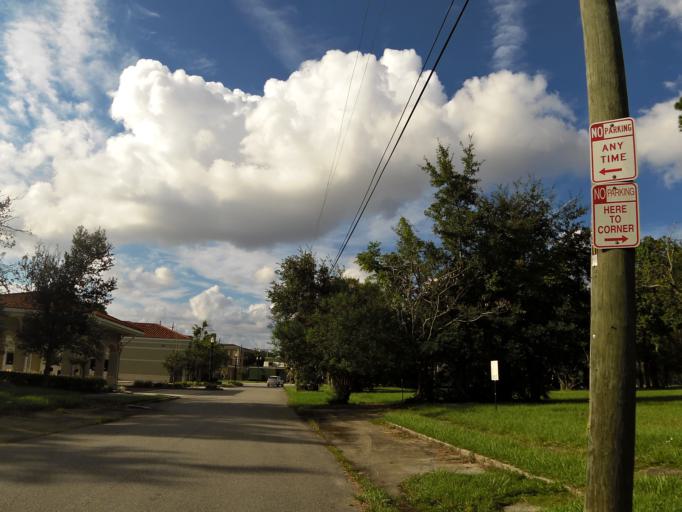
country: US
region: Florida
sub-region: Duval County
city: Jacksonville
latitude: 30.3050
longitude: -81.6510
